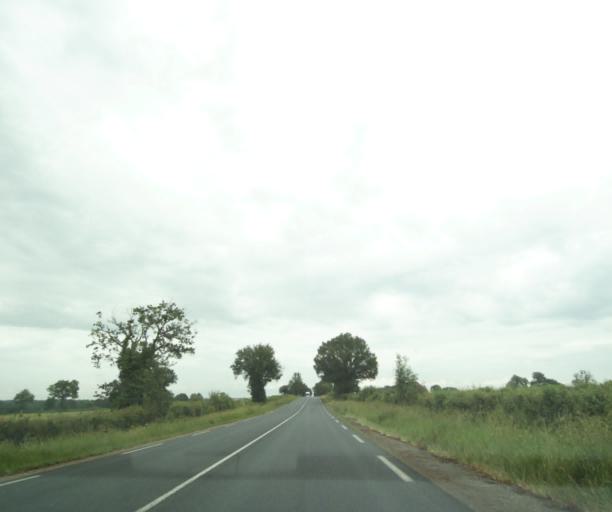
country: FR
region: Poitou-Charentes
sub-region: Departement des Deux-Sevres
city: Viennay
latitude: 46.7381
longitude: -0.2333
